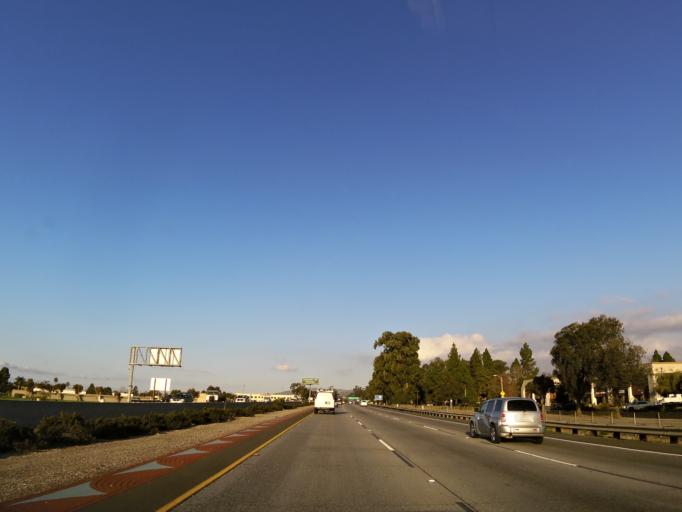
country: US
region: California
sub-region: Ventura County
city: El Rio
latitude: 34.2581
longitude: -119.2214
